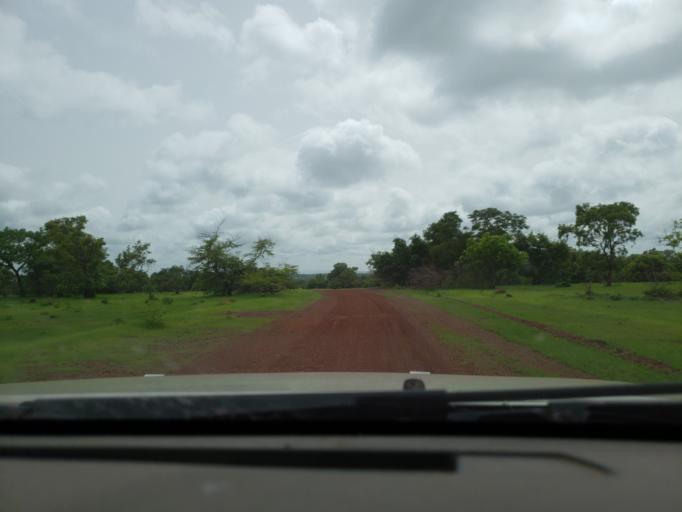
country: ML
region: Koulikoro
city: Kangaba
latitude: 12.1109
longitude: -8.5590
